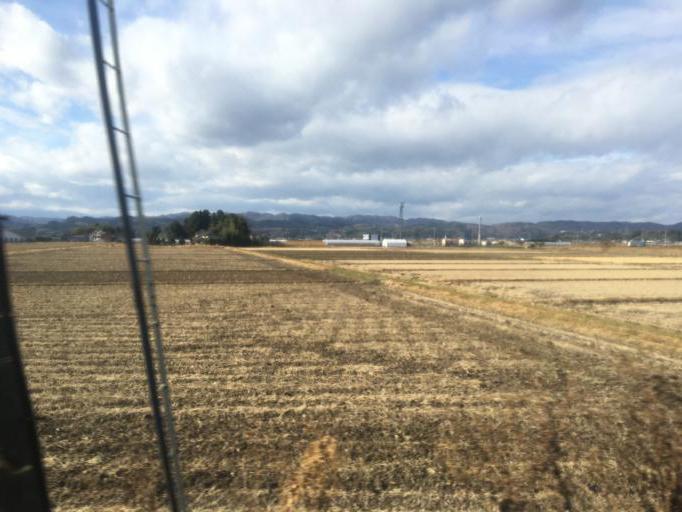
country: JP
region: Miyagi
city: Iwanuma
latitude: 38.1377
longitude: 140.8780
